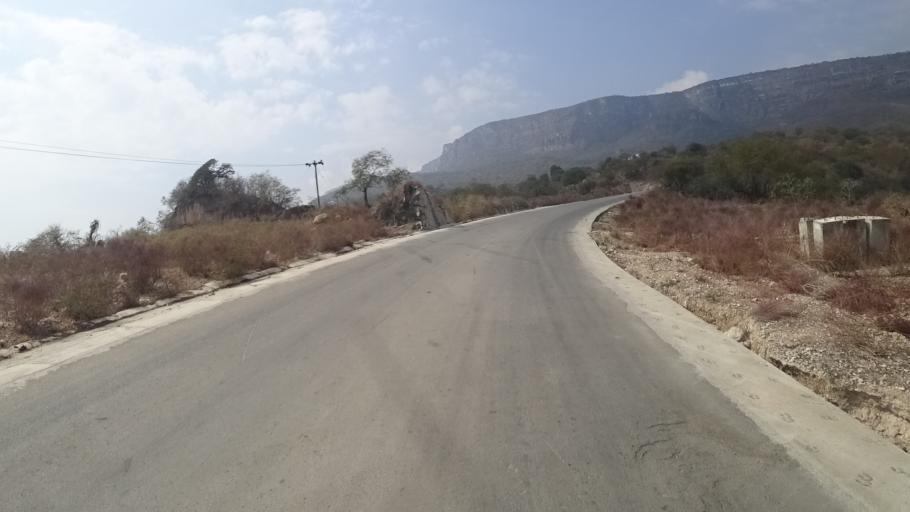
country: YE
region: Al Mahrah
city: Hawf
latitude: 16.7102
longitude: 53.2561
